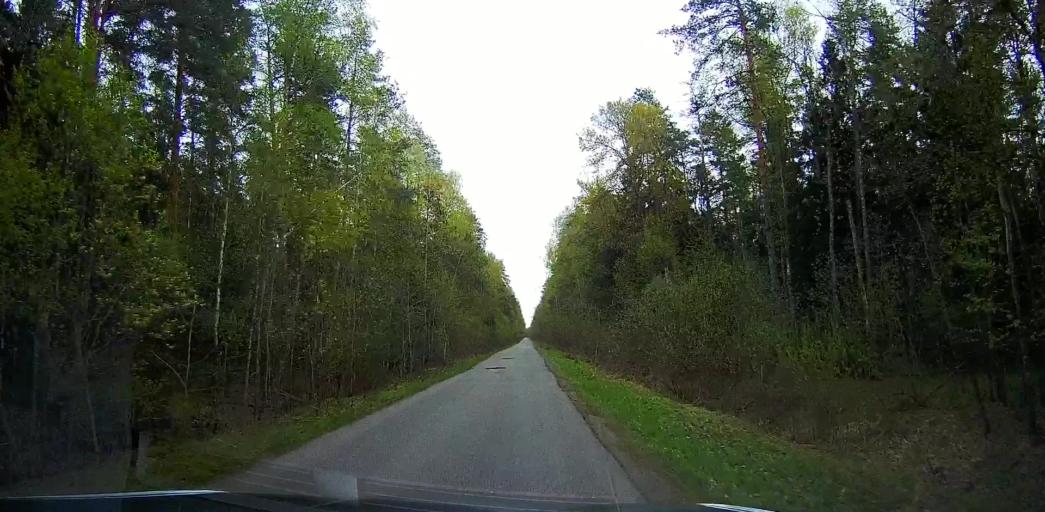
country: RU
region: Moskovskaya
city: Malyshevo
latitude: 55.5480
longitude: 38.3644
